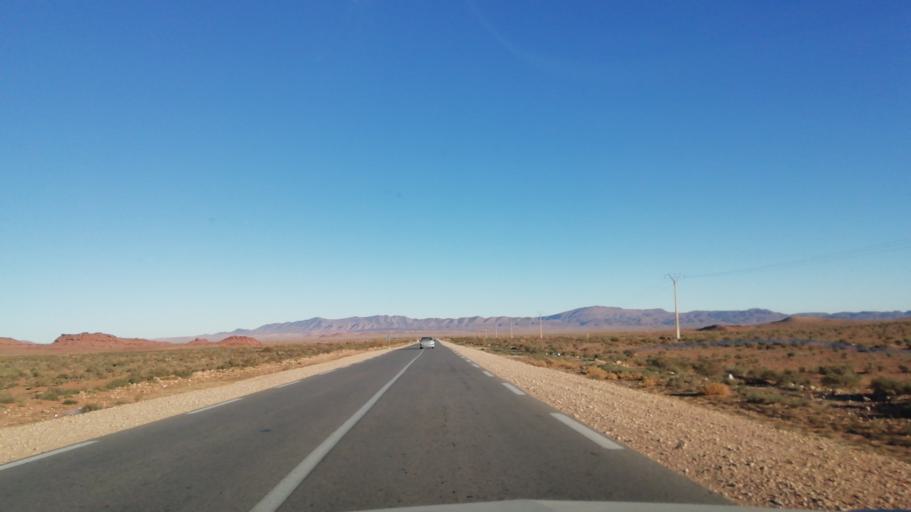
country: DZ
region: El Bayadh
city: El Abiodh Sidi Cheikh
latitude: 33.1705
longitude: 0.4942
